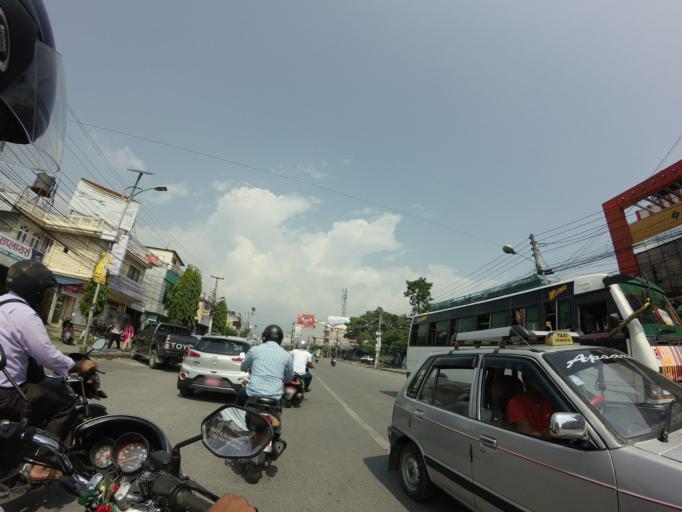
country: NP
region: Western Region
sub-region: Gandaki Zone
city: Pokhara
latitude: 28.2123
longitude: 83.9851
